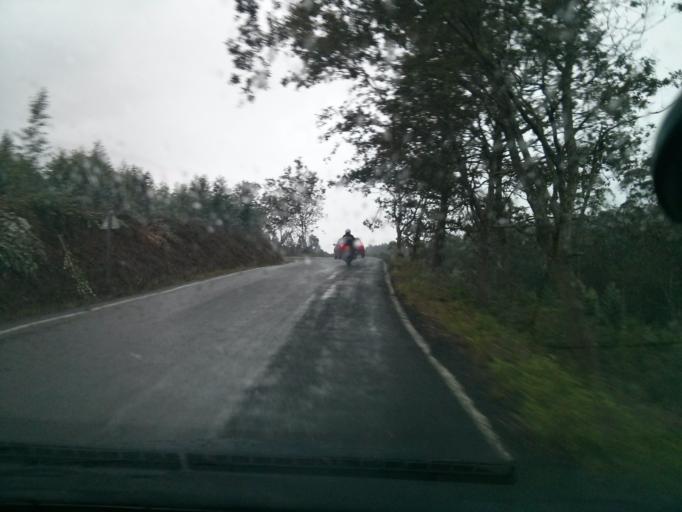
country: ES
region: Galicia
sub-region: Provincia da Coruna
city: Outes
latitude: 42.8310
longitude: -8.8670
